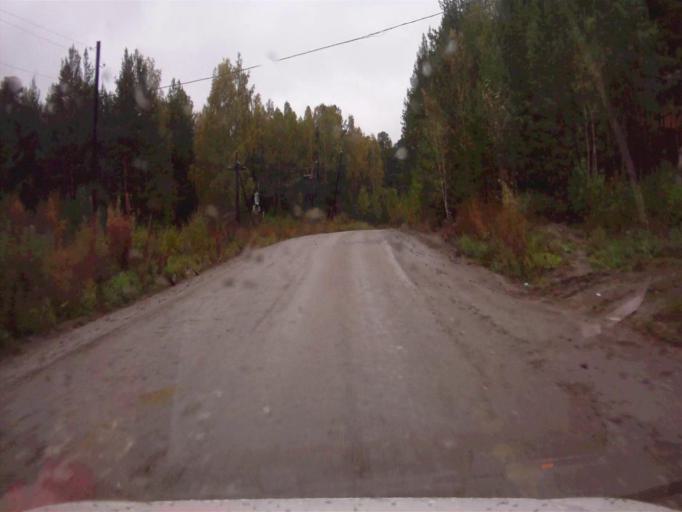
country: RU
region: Chelyabinsk
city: Kyshtym
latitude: 55.7434
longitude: 60.4935
